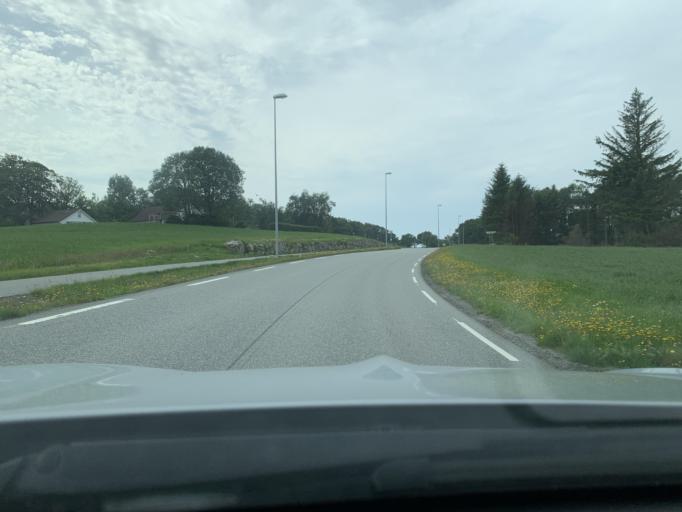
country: NO
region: Rogaland
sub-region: Time
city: Bryne
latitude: 58.7408
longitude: 5.6899
